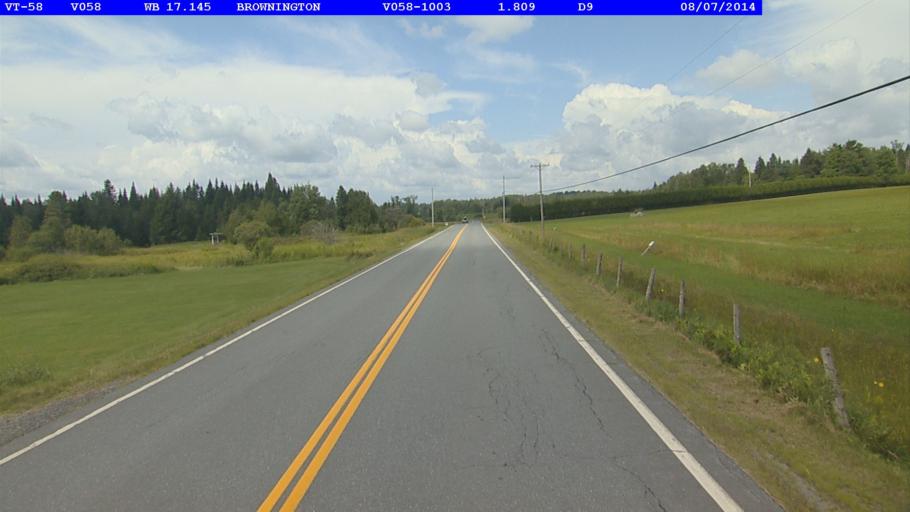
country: US
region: Vermont
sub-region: Orleans County
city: Newport
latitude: 44.7965
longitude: -72.1122
